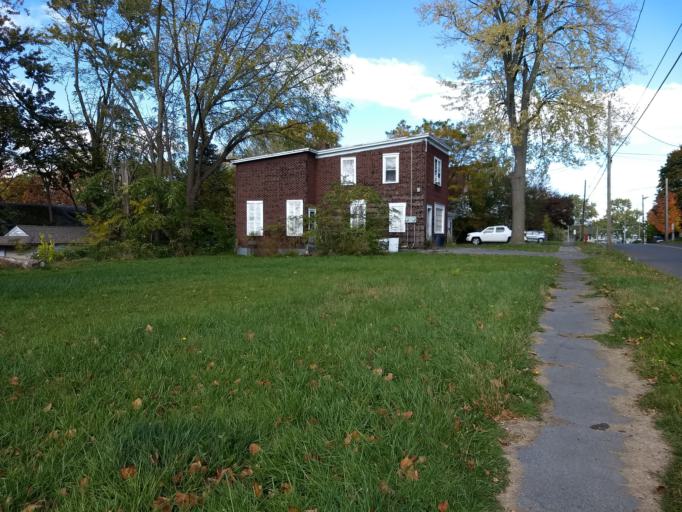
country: US
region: New York
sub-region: Onondaga County
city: Galeville
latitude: 43.0734
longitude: -76.1546
